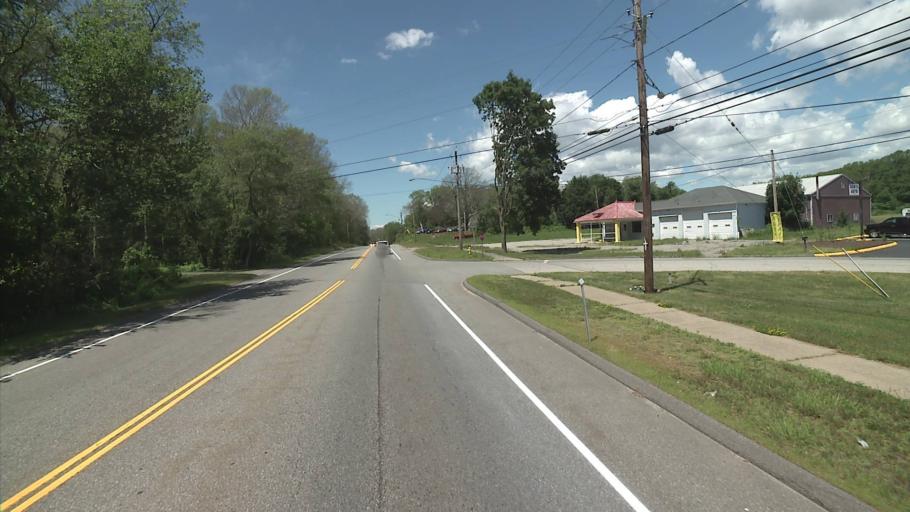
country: US
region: Connecticut
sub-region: New London County
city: Long Hill
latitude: 41.3827
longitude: -72.0287
